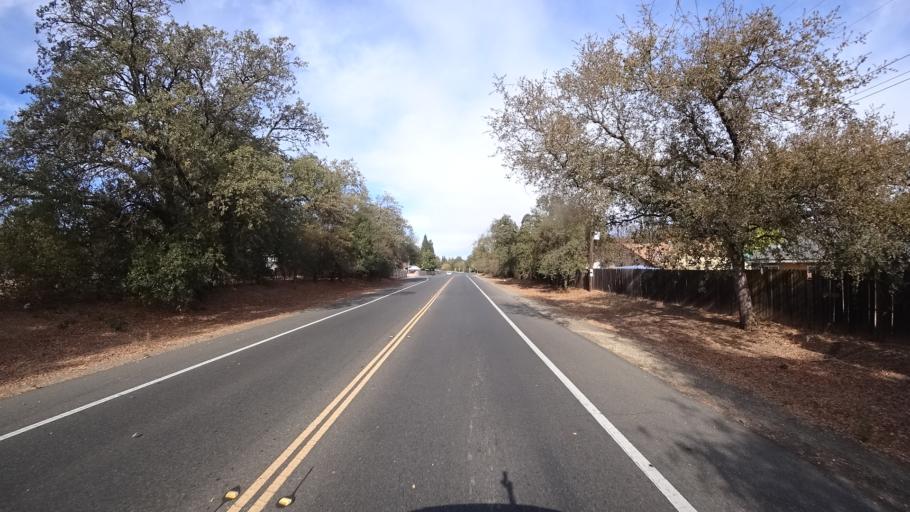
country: US
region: California
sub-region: Sacramento County
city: Citrus Heights
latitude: 38.7032
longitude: -121.2624
